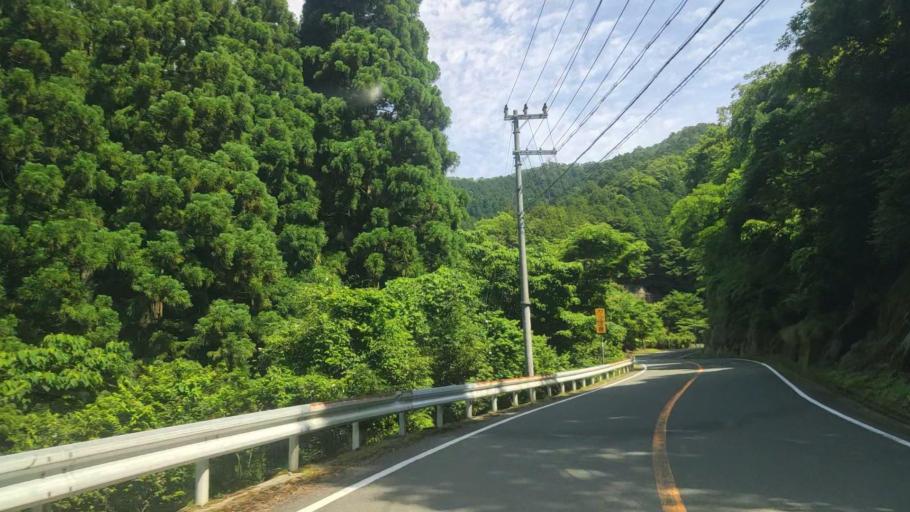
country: JP
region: Hyogo
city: Toyooka
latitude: 35.6348
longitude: 134.7805
